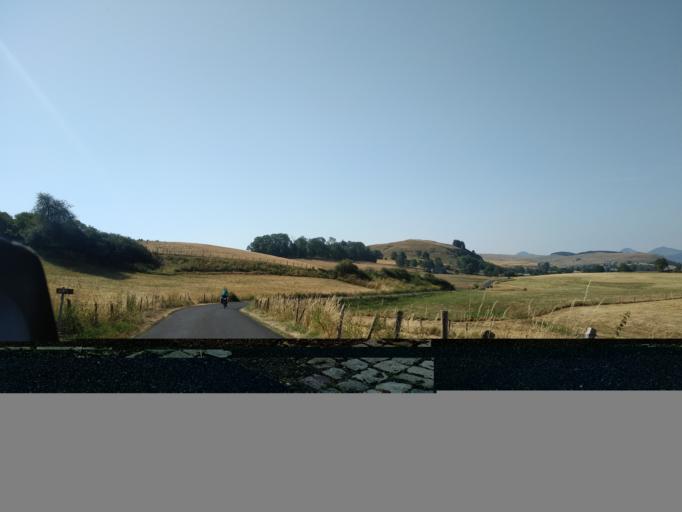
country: FR
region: Auvergne
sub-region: Departement du Cantal
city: Riom-es-Montagnes
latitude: 45.2536
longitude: 2.7436
